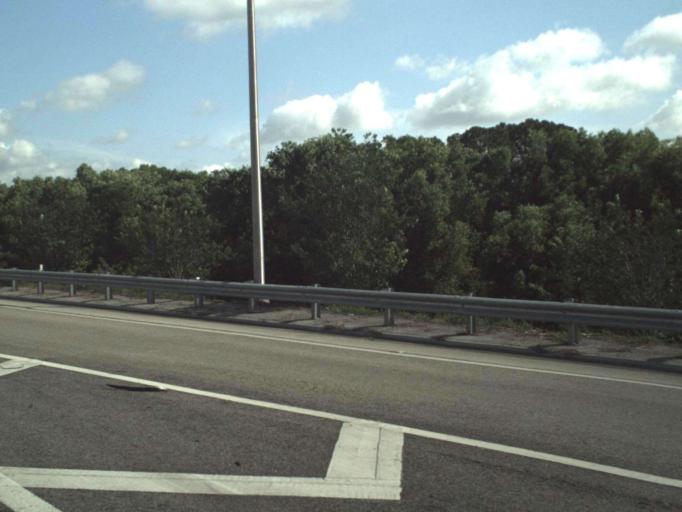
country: US
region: Florida
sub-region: Palm Beach County
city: North Palm Beach
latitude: 26.8424
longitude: -80.1035
